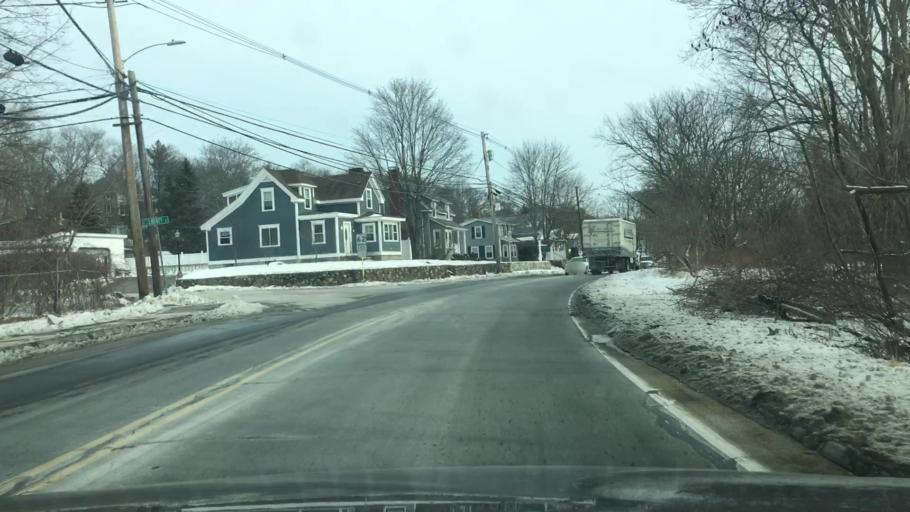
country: US
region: Massachusetts
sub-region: Essex County
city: Middleton
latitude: 42.5964
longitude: -71.0015
